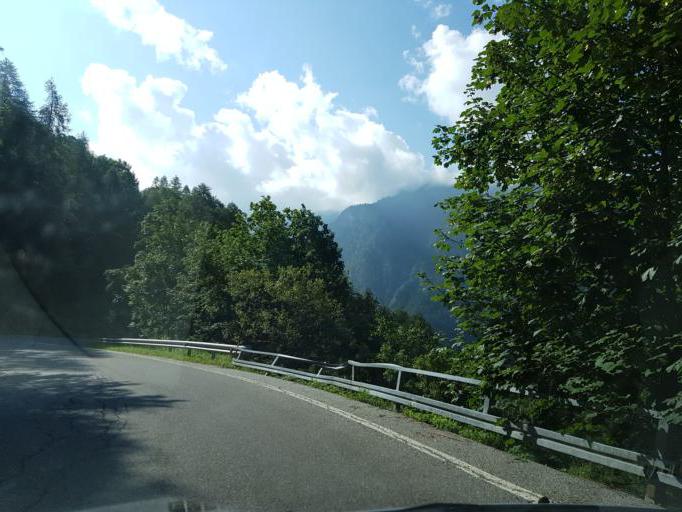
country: IT
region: Piedmont
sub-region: Provincia di Cuneo
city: Casteldelfino
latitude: 44.6001
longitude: 7.0669
